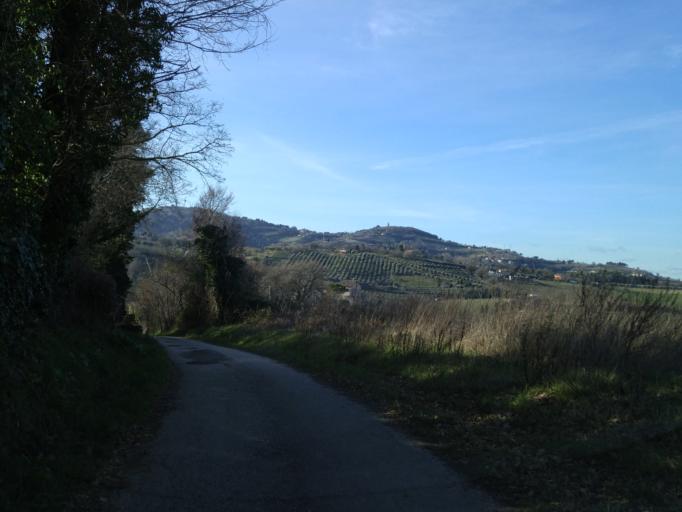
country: IT
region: The Marches
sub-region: Provincia di Pesaro e Urbino
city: Cartoceto
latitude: 43.7735
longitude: 12.8923
